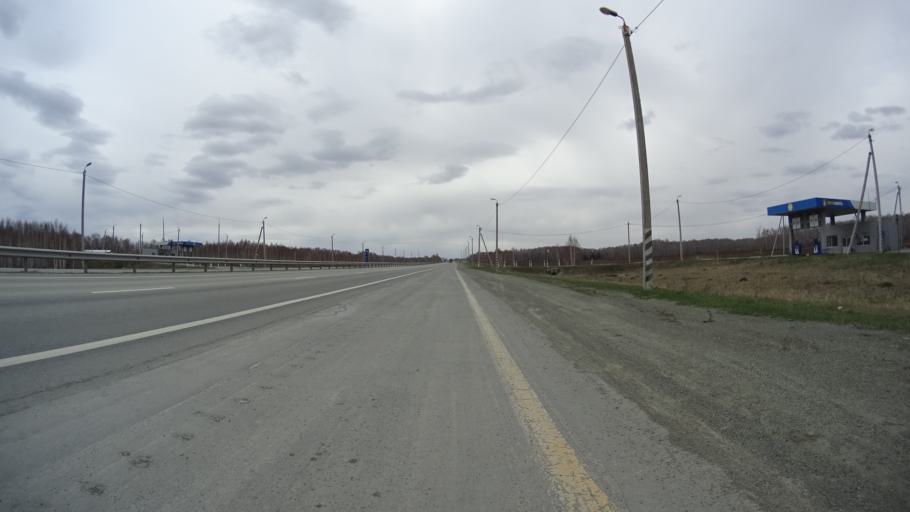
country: RU
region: Chelyabinsk
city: Yemanzhelinka
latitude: 54.8342
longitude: 61.3123
